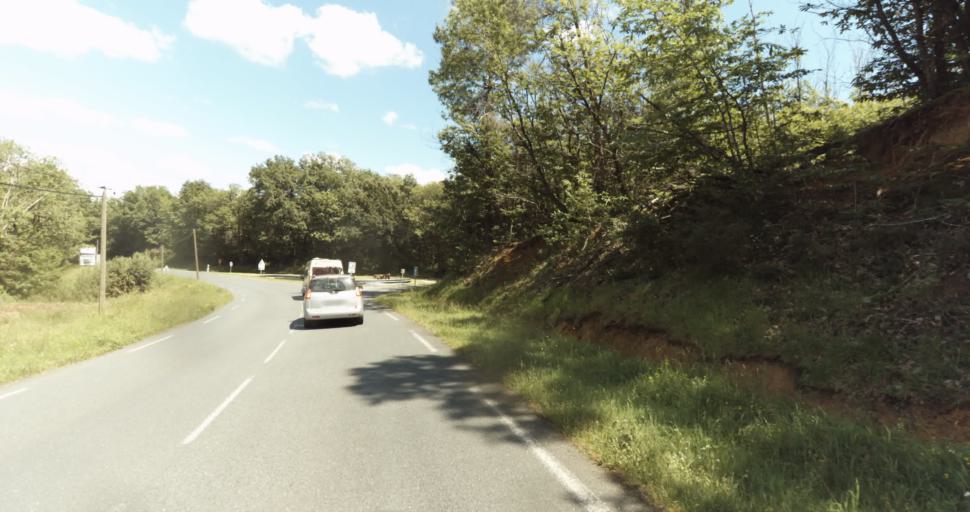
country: FR
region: Aquitaine
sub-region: Departement de la Dordogne
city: Le Bugue
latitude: 44.8413
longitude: 0.8778
